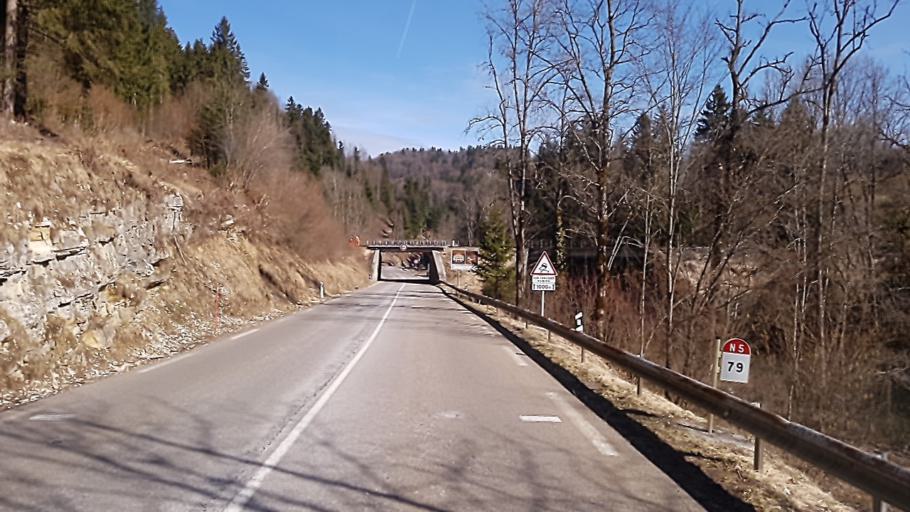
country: FR
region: Franche-Comte
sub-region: Departement du Jura
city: Champagnole
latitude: 46.6602
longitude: 5.9458
